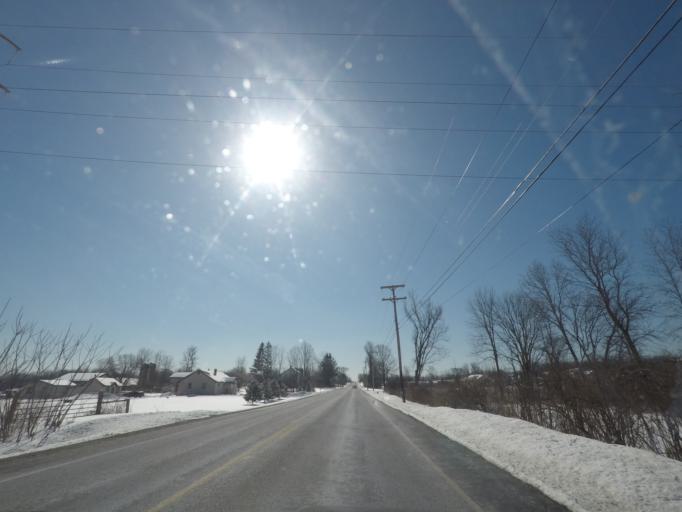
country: US
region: New York
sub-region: Saratoga County
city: Ballston Spa
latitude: 42.9590
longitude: -73.8290
